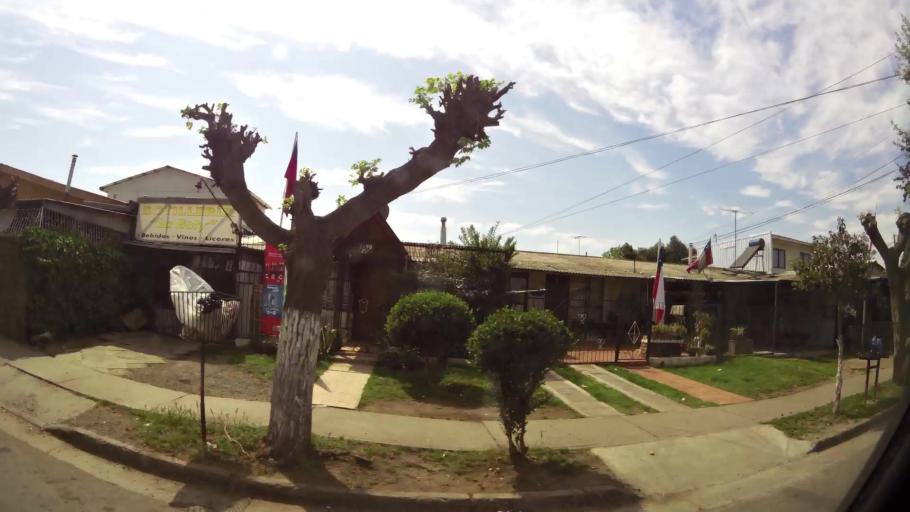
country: CL
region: Santiago Metropolitan
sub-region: Provincia de Talagante
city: Talagante
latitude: -33.6642
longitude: -70.9195
